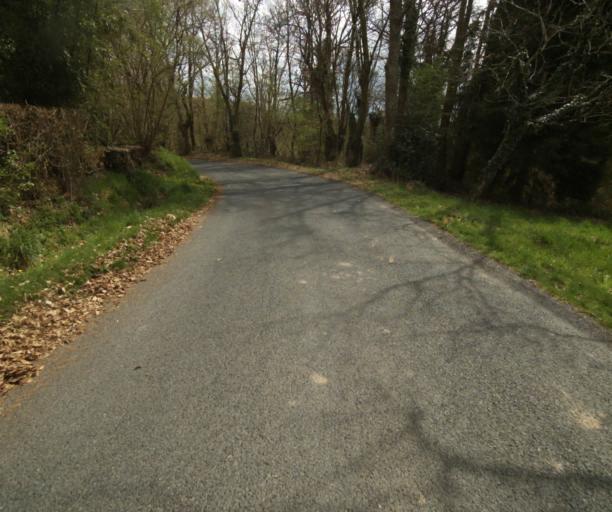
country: FR
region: Limousin
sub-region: Departement de la Correze
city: Laguenne
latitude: 45.2537
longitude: 1.8750
